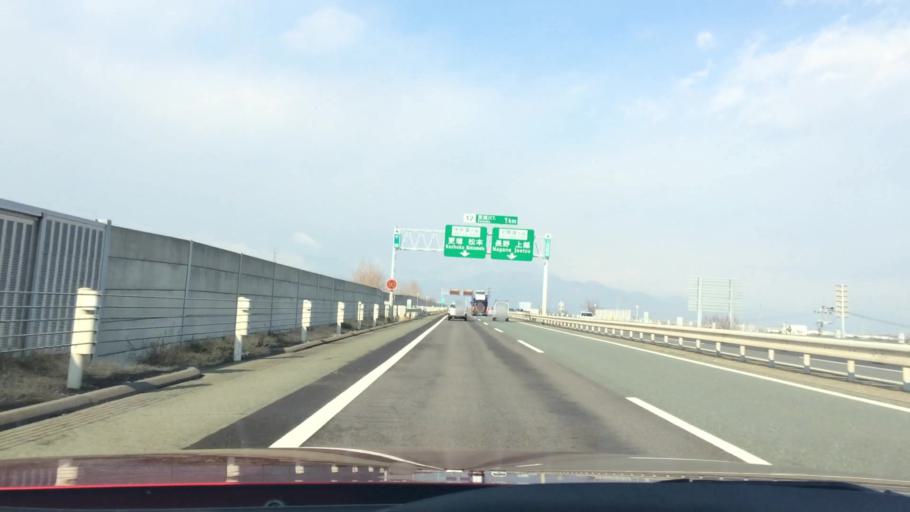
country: JP
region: Nagano
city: Nagano-shi
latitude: 36.5411
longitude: 138.1395
